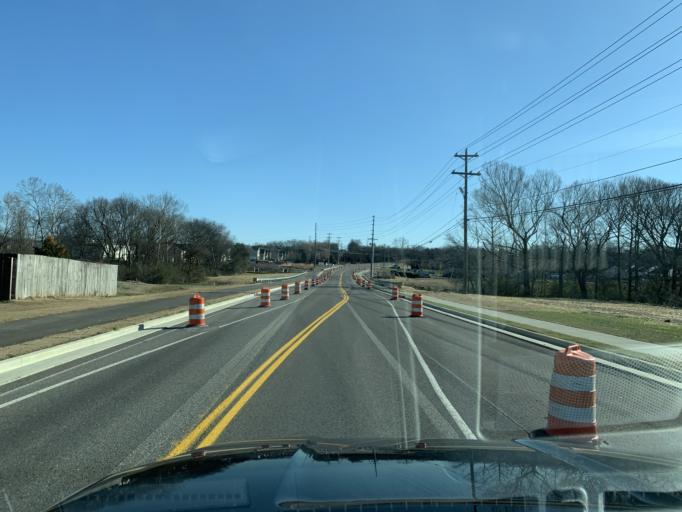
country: US
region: Tennessee
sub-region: Maury County
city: Spring Hill
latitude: 35.7528
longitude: -86.8758
